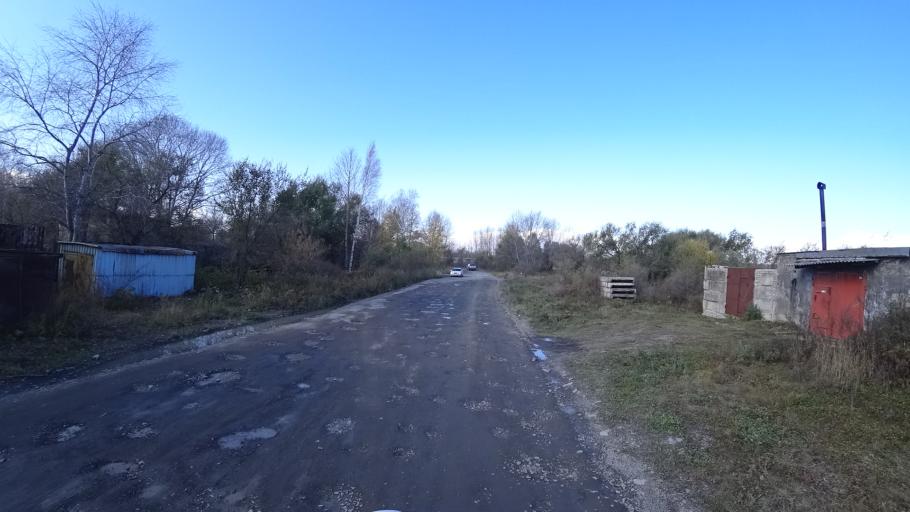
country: RU
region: Khabarovsk Krai
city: Amursk
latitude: 50.1021
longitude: 136.5061
